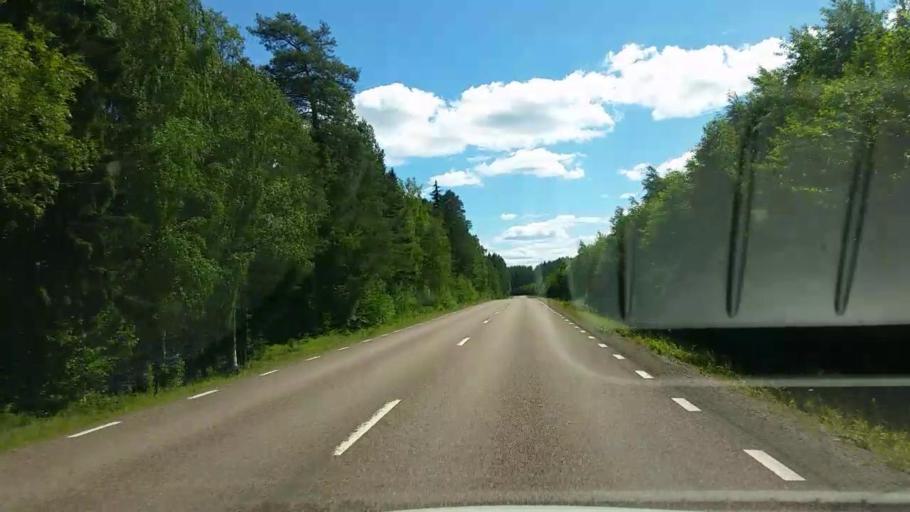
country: SE
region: Dalarna
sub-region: Faluns Kommun
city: Svardsjo
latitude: 60.9647
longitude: 15.6919
